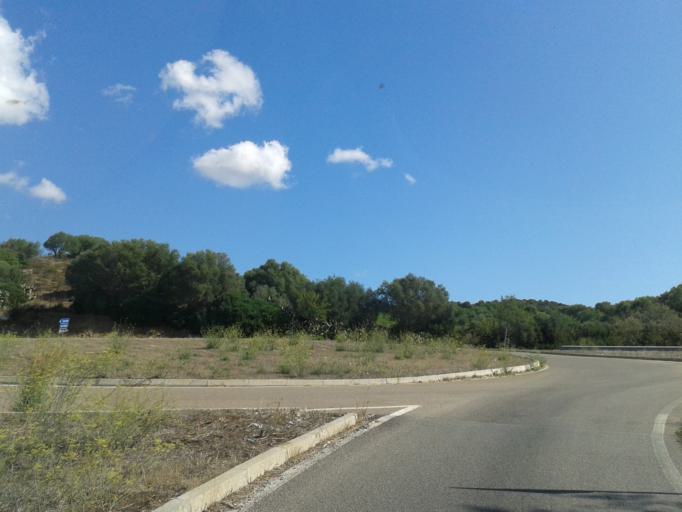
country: IT
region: Sardinia
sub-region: Provincia di Cagliari
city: Villasimius
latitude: 39.1534
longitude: 9.5162
